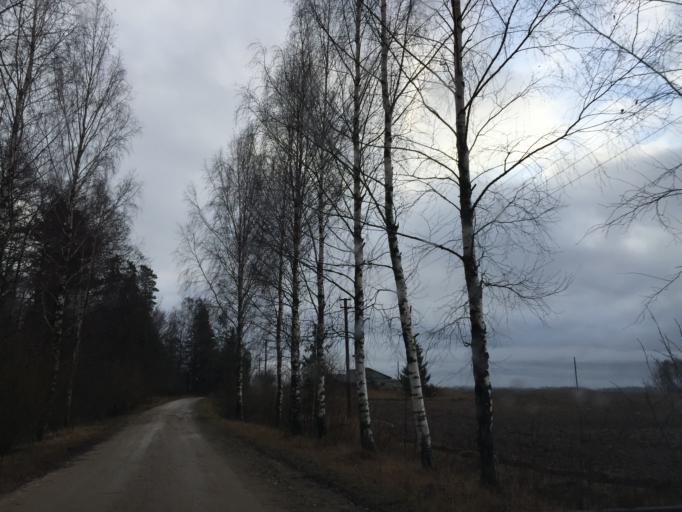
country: LV
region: Vainode
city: Vainode
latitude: 56.6068
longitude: 21.7992
